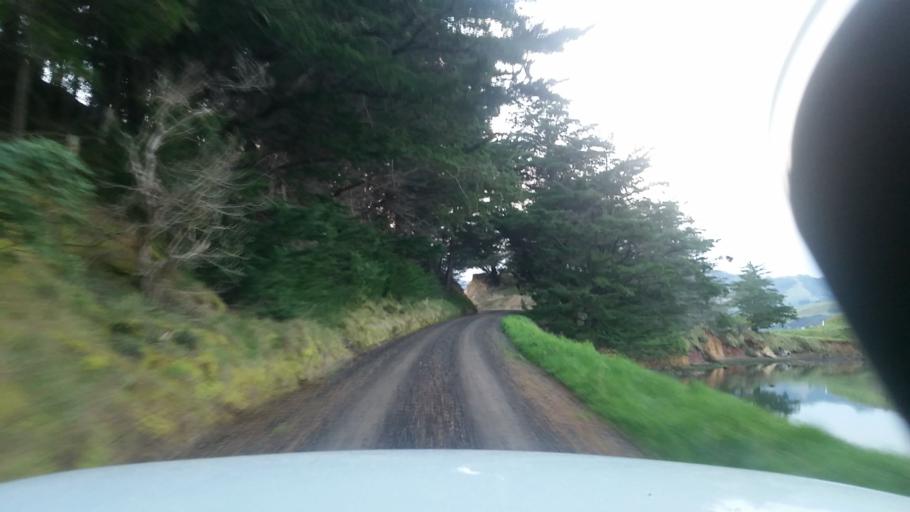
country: NZ
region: Canterbury
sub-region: Christchurch City
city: Christchurch
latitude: -43.7630
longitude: 172.9257
